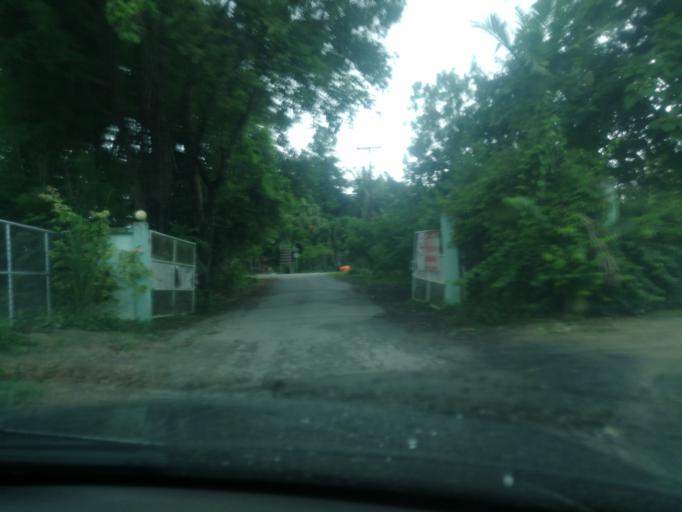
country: TH
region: Chiang Mai
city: San Pa Tong
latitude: 18.6471
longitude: 98.8503
